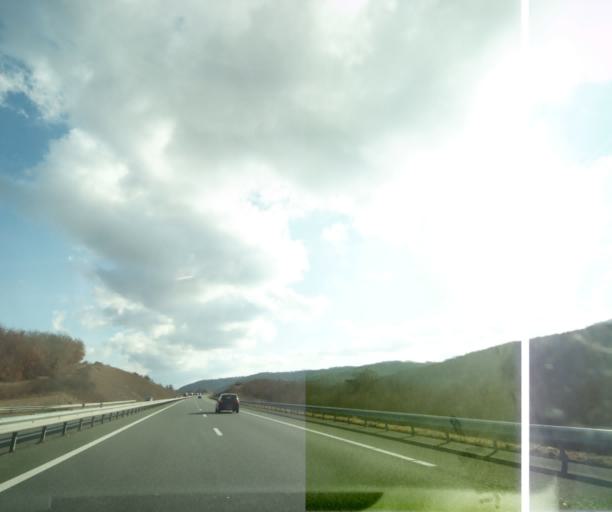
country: FR
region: Midi-Pyrenees
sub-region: Departement du Lot
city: Souillac
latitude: 44.8188
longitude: 1.4990
